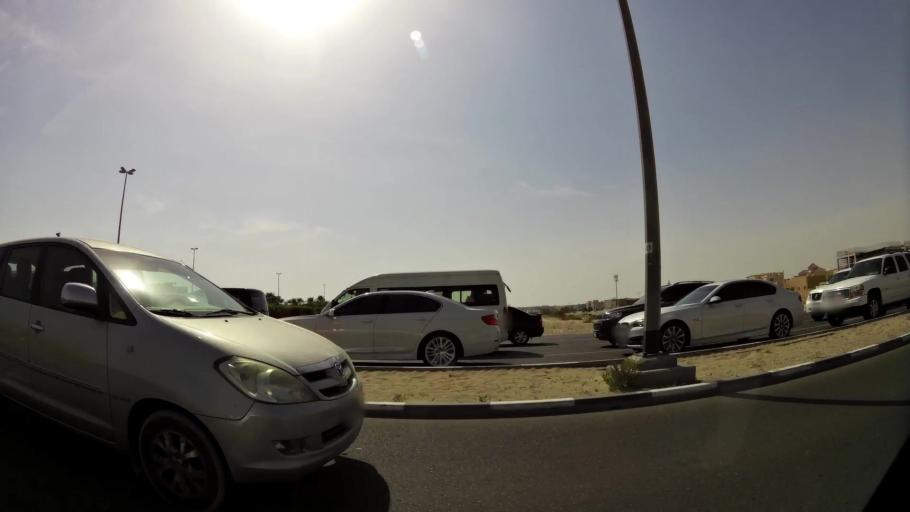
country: AE
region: Ash Shariqah
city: Sharjah
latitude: 25.2084
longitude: 55.4207
